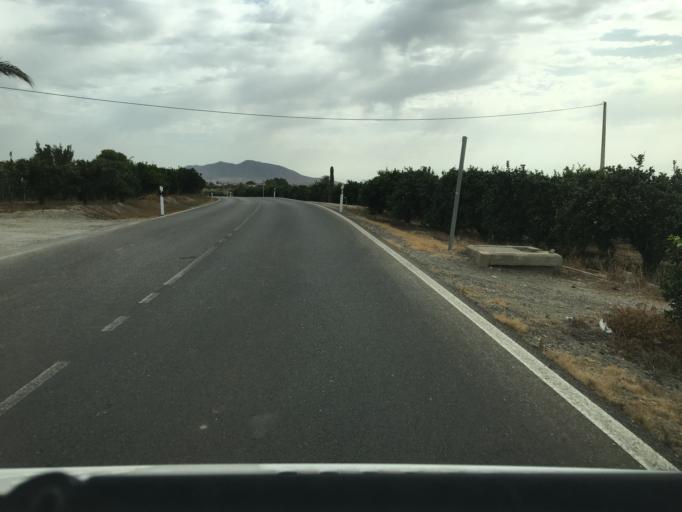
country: ES
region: Andalusia
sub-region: Provincia de Almeria
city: Huercal-Overa
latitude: 37.4095
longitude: -1.9221
